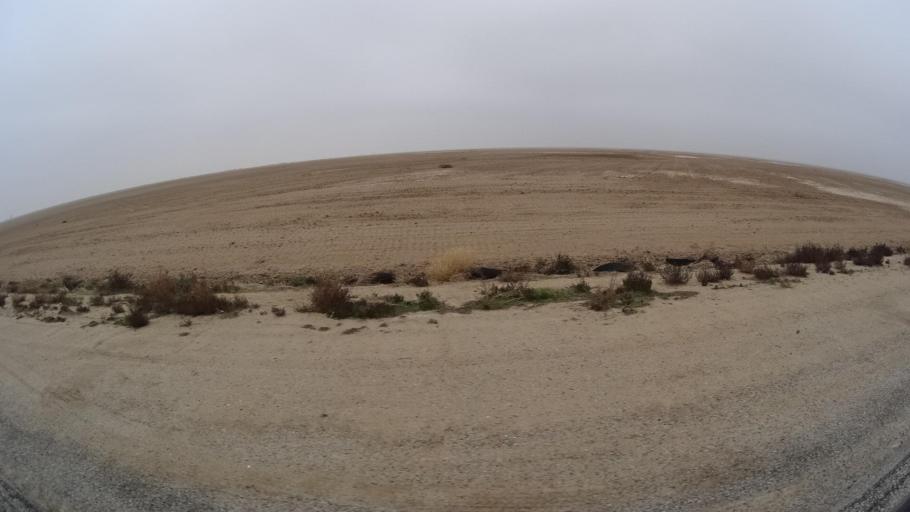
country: US
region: California
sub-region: Kern County
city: Maricopa
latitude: 35.1296
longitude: -119.2567
